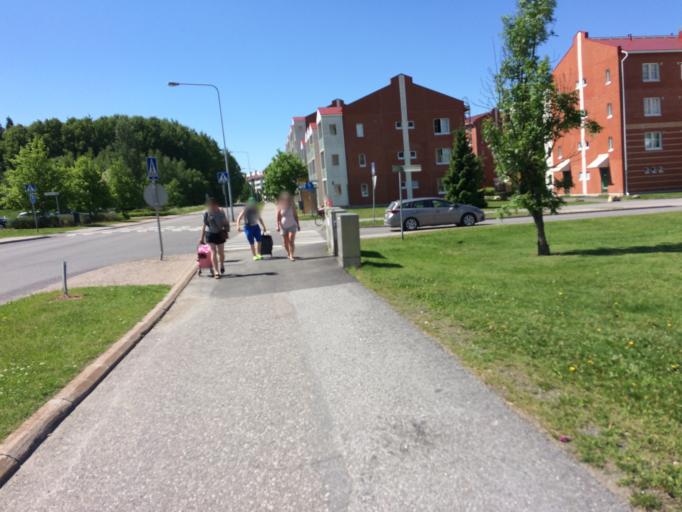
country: FI
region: Varsinais-Suomi
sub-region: Turku
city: Turku
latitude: 60.4719
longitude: 22.3167
